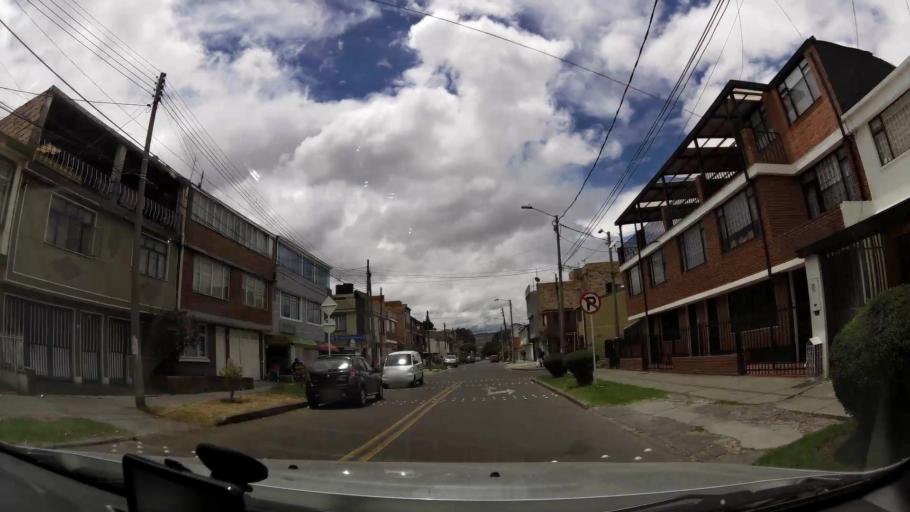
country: CO
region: Bogota D.C.
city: Bogota
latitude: 4.6018
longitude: -74.1124
